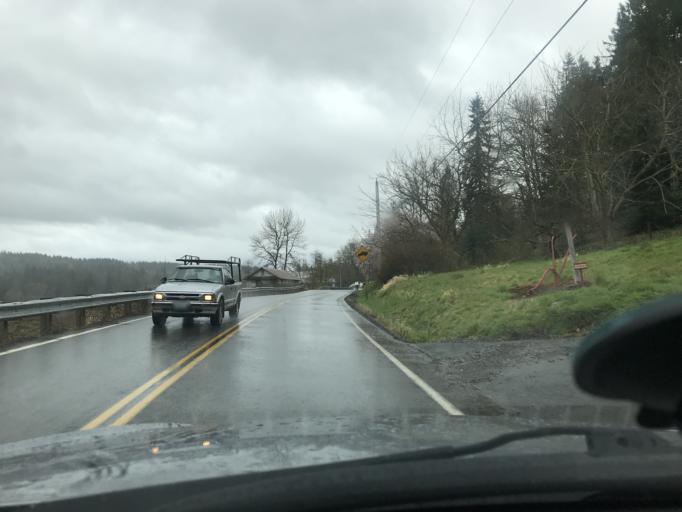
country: US
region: Washington
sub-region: King County
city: Ames Lake
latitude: 47.6698
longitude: -121.9755
